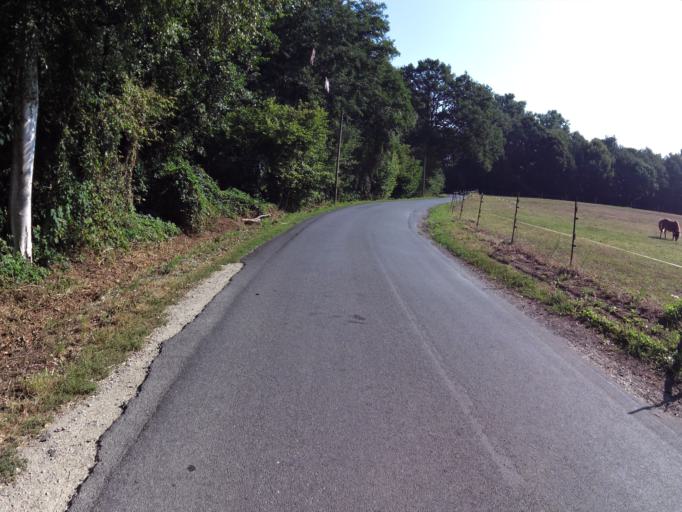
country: DE
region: North Rhine-Westphalia
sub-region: Regierungsbezirk Detmold
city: Harsewinkel
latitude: 51.9483
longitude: 8.1914
